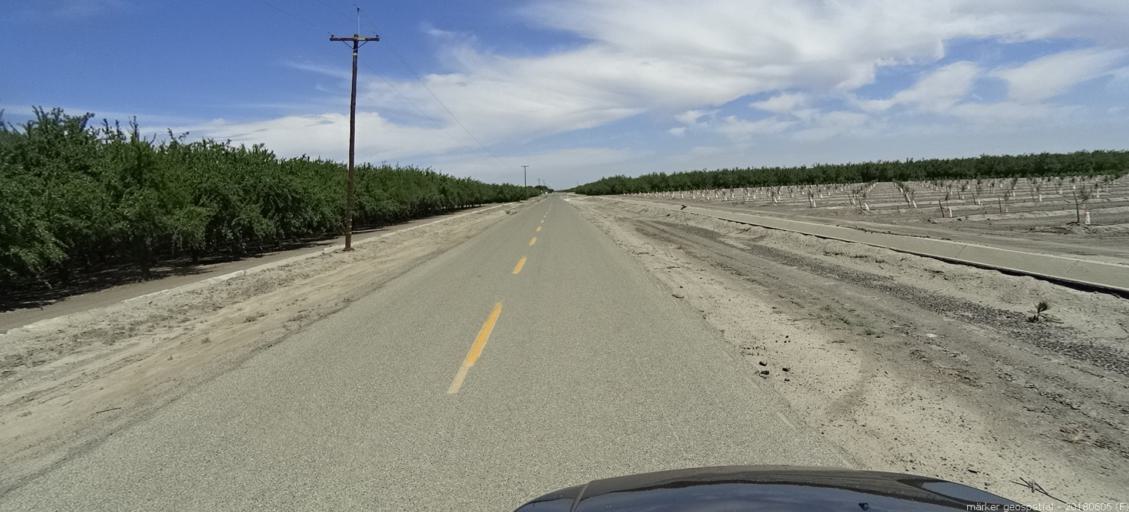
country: US
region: California
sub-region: Fresno County
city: Firebaugh
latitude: 36.8431
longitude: -120.3911
